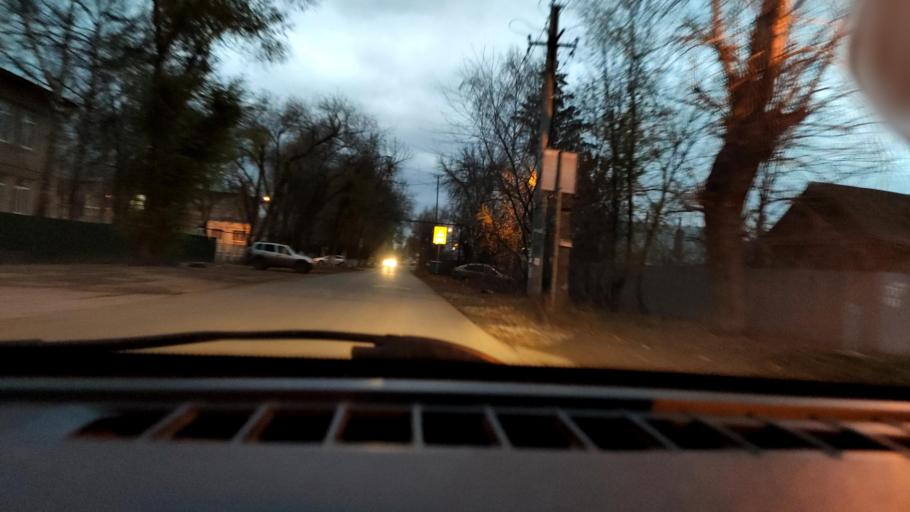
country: RU
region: Samara
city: Petra-Dubrava
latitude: 53.2498
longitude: 50.3284
